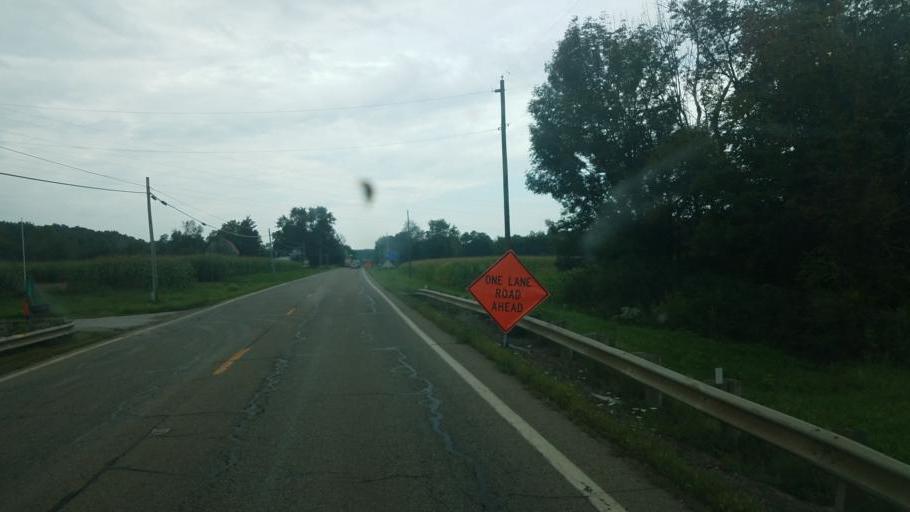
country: US
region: Ohio
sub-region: Knox County
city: Mount Vernon
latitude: 40.4376
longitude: -82.4469
